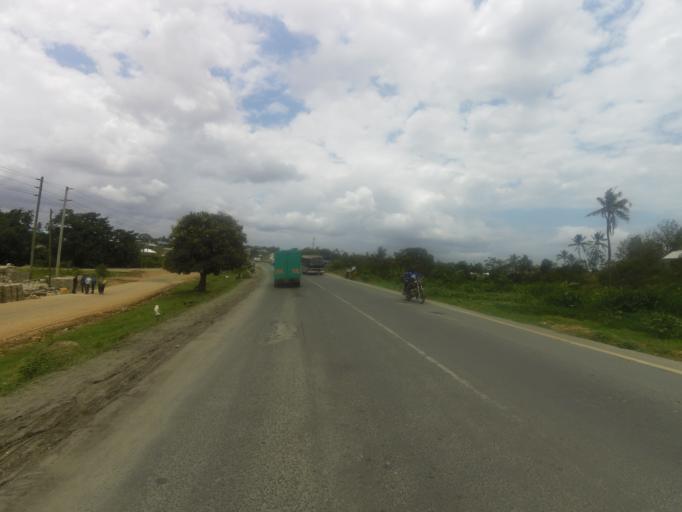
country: TZ
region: Pwani
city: Vikindu
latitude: -6.9359
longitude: 39.2735
